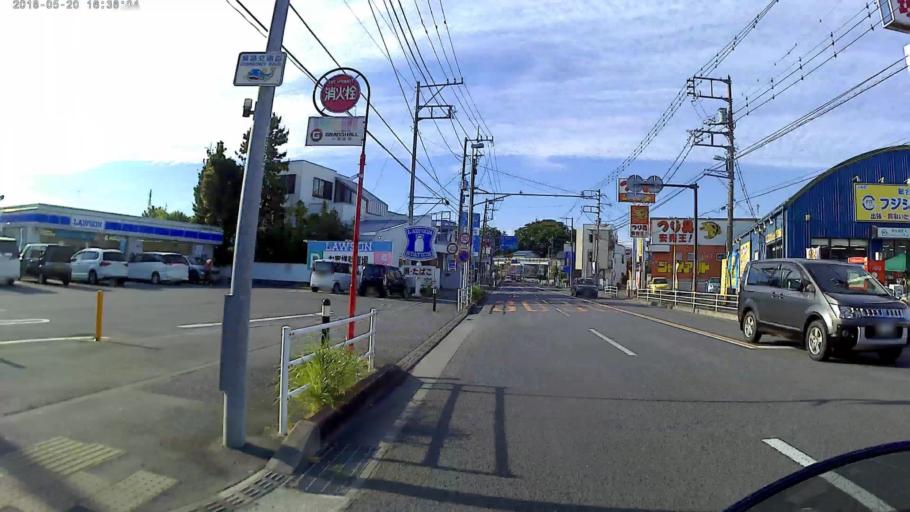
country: JP
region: Kanagawa
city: Odawara
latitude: 35.2698
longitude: 139.1588
